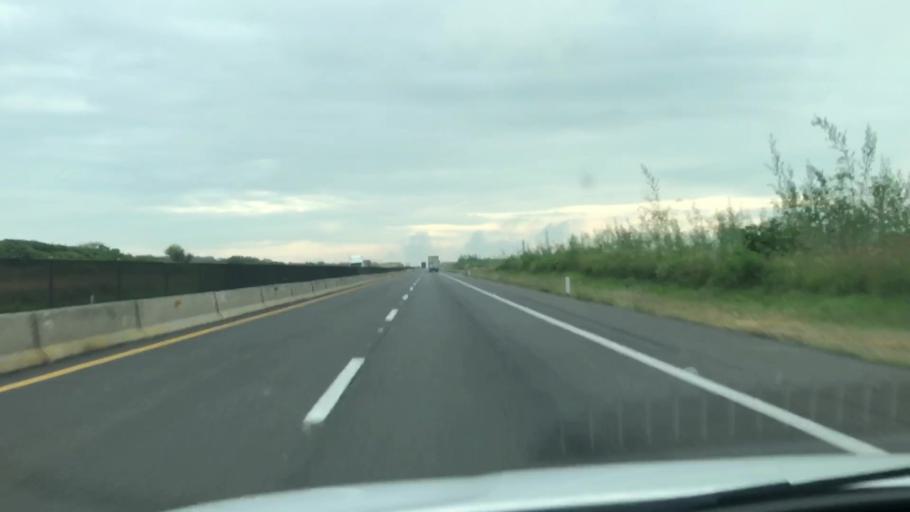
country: MX
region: Jalisco
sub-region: San Juan de los Lagos
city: Colonia Santa Cecilia (La Sauceda)
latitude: 21.1805
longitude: -102.3716
